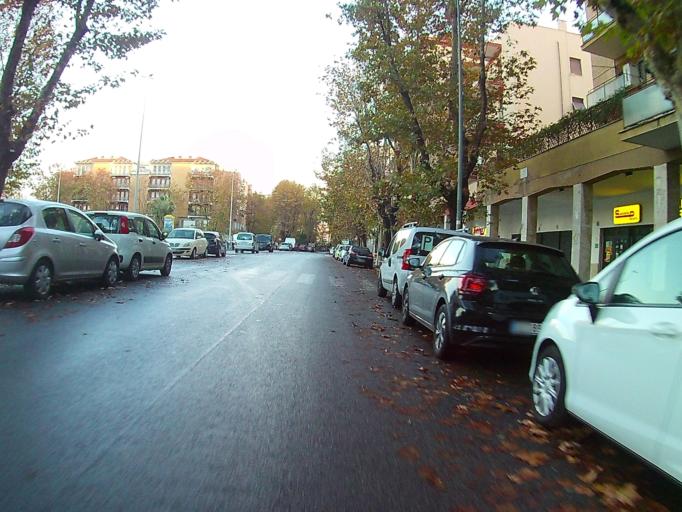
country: IT
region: Latium
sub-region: Citta metropolitana di Roma Capitale
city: Lido di Ostia
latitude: 41.7271
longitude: 12.2938
